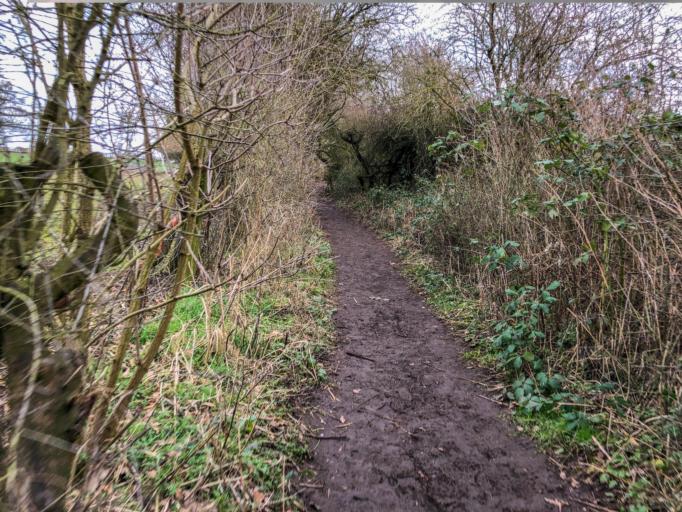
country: GB
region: England
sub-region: Warwickshire
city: Kenilworth
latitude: 52.3495
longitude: -1.6048
